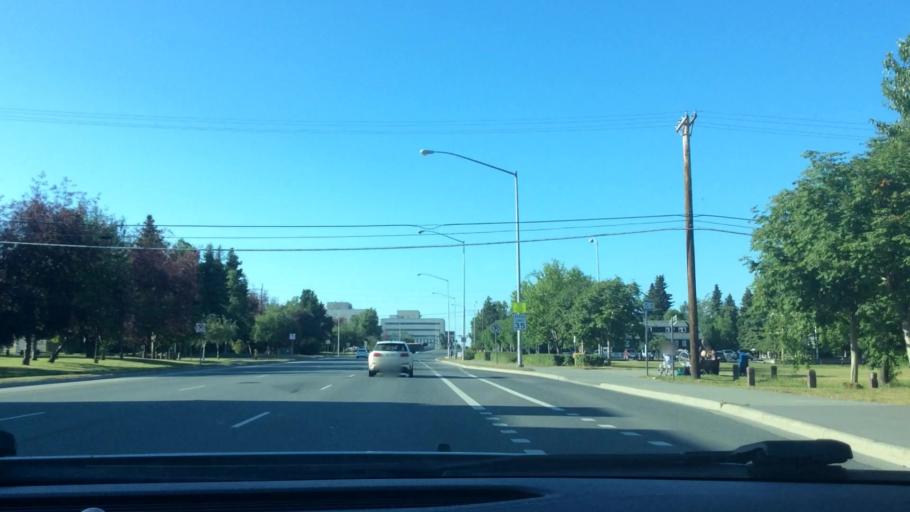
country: US
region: Alaska
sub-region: Anchorage Municipality
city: Anchorage
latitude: 61.2098
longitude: -149.8831
